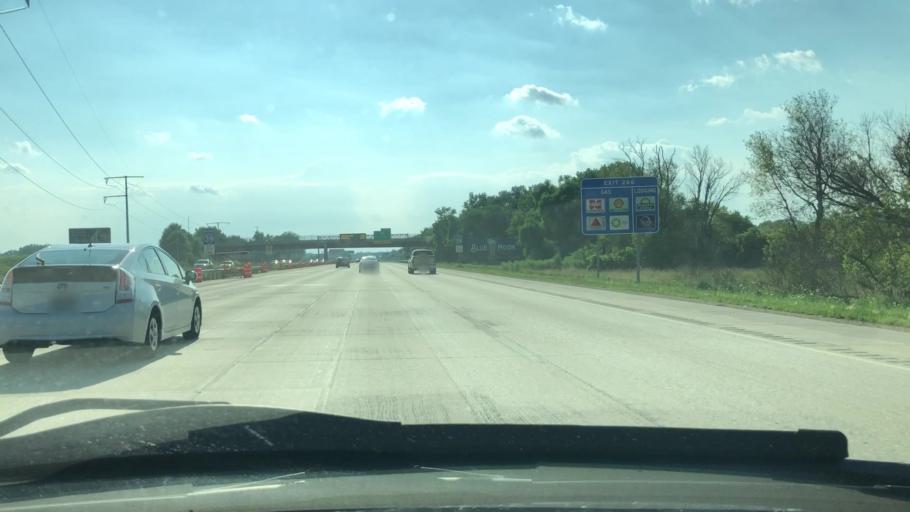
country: US
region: Wisconsin
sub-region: Dane County
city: McFarland
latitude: 43.0481
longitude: -89.2872
